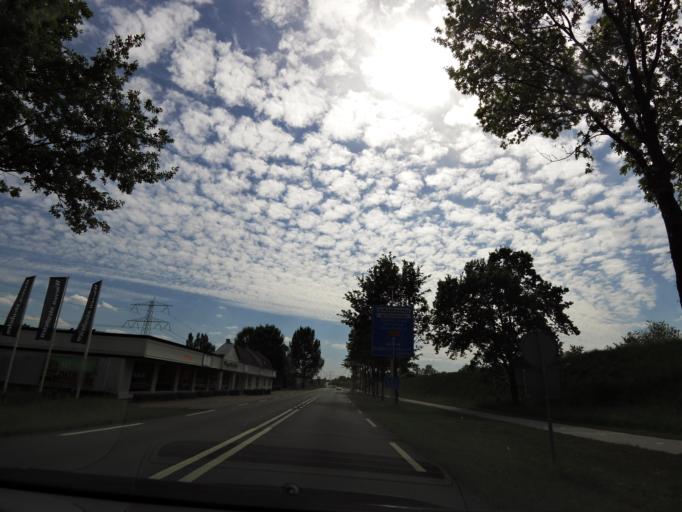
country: NL
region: Limburg
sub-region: Gemeente Leudal
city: Haelen
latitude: 51.2355
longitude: 5.9636
